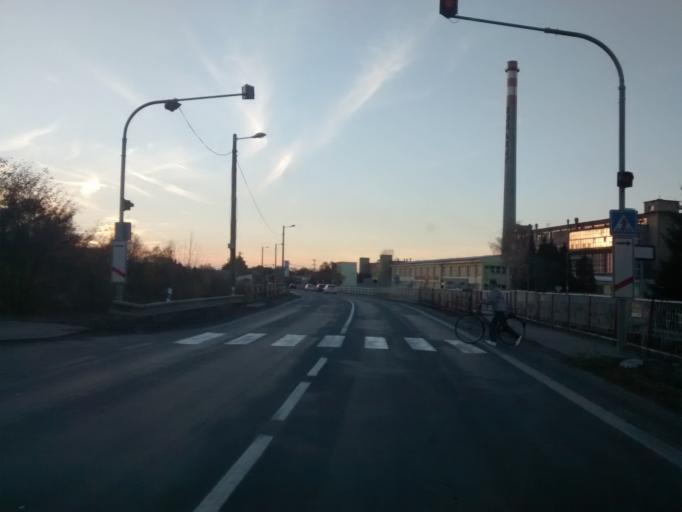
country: CZ
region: Zlin
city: Zubri
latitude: 49.4611
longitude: 18.0936
